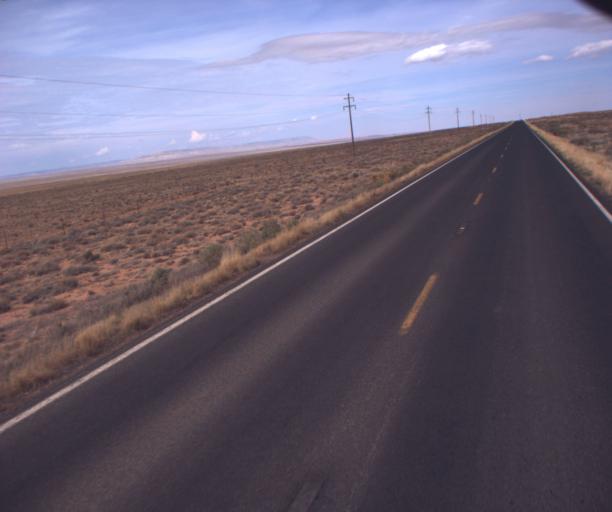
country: US
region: Arizona
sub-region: Apache County
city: Ganado
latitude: 35.9038
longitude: -109.6114
